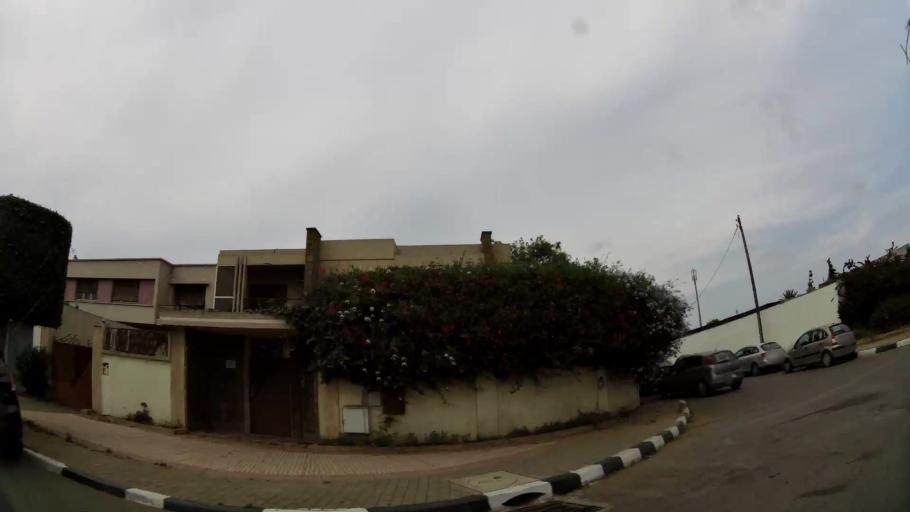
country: MA
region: Rabat-Sale-Zemmour-Zaer
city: Sale
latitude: 34.0301
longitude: -6.8110
